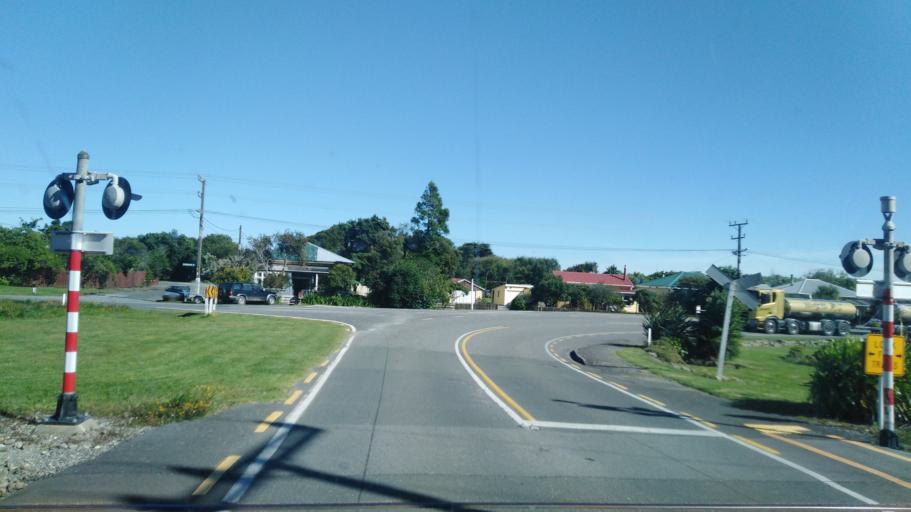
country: NZ
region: West Coast
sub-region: Buller District
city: Westport
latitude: -41.6324
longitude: 171.8519
